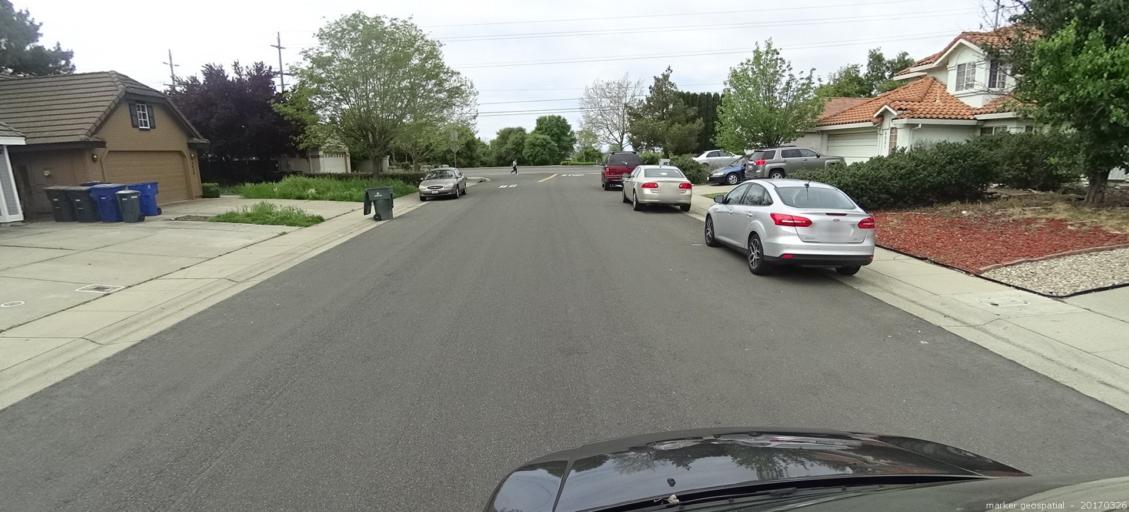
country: US
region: California
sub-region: Sacramento County
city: Laguna
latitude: 38.4419
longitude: -121.4441
